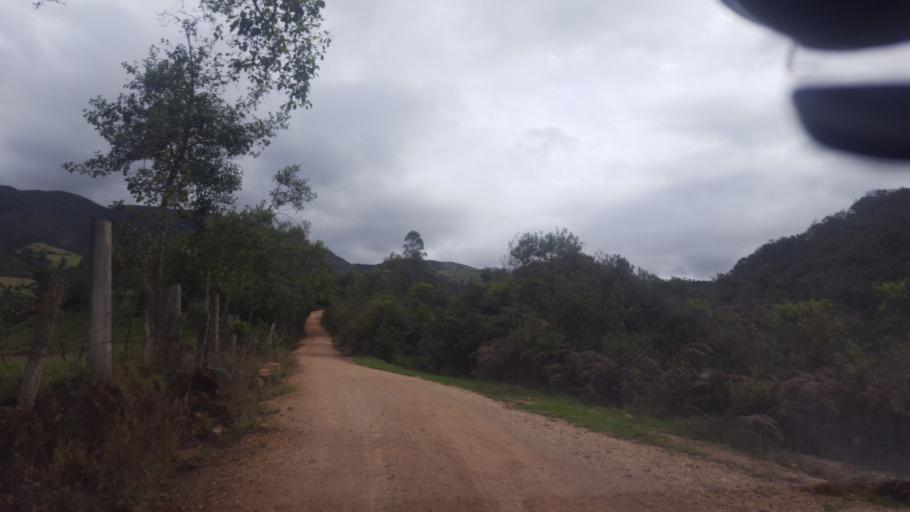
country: CO
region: Boyaca
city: Cerinza
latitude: 5.9888
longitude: -72.9492
